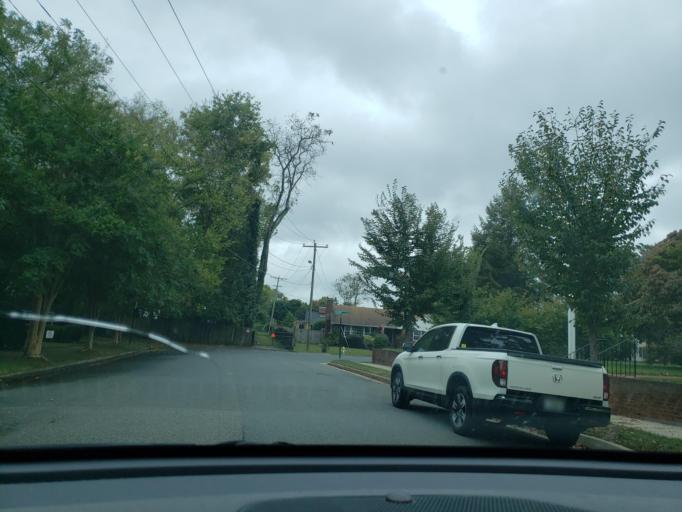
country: US
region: Virginia
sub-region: City of Fredericksburg
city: Fredericksburg
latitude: 38.2985
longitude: -77.4746
